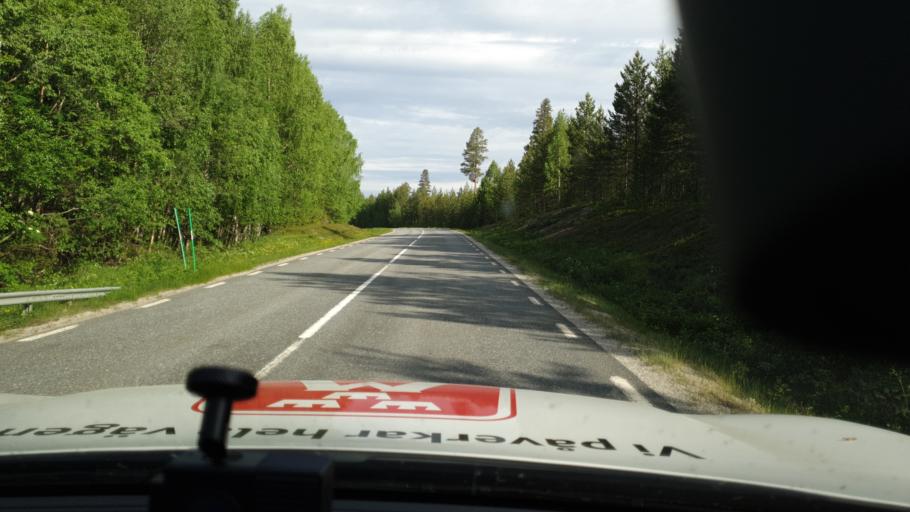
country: SE
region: Vaesterbotten
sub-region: Lycksele Kommun
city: Lycksele
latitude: 64.4508
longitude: 18.9337
